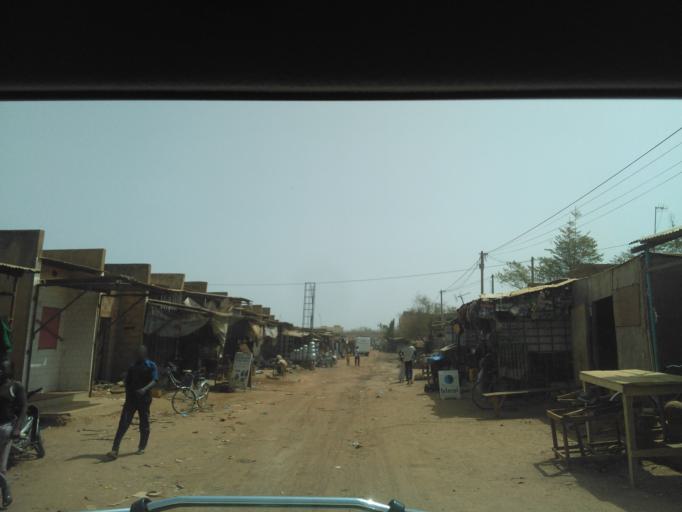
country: BF
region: Centre
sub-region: Kadiogo Province
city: Ouagadougou
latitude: 12.3896
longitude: -1.5659
